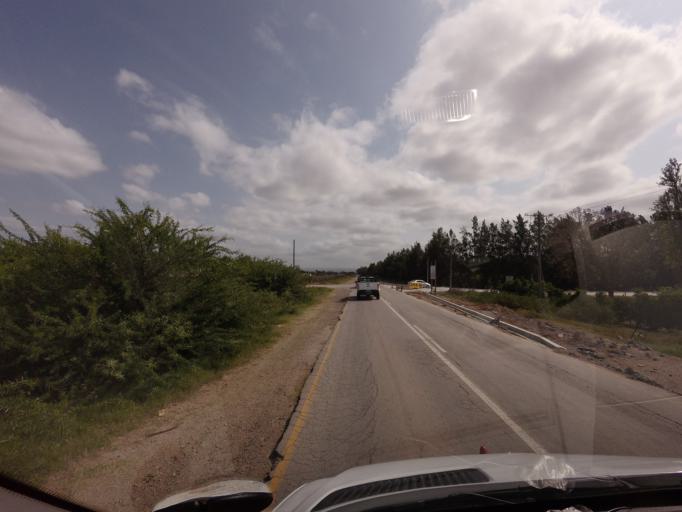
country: ZA
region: Eastern Cape
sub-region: Cacadu District Municipality
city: Kirkwood
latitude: -33.5361
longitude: 25.6908
